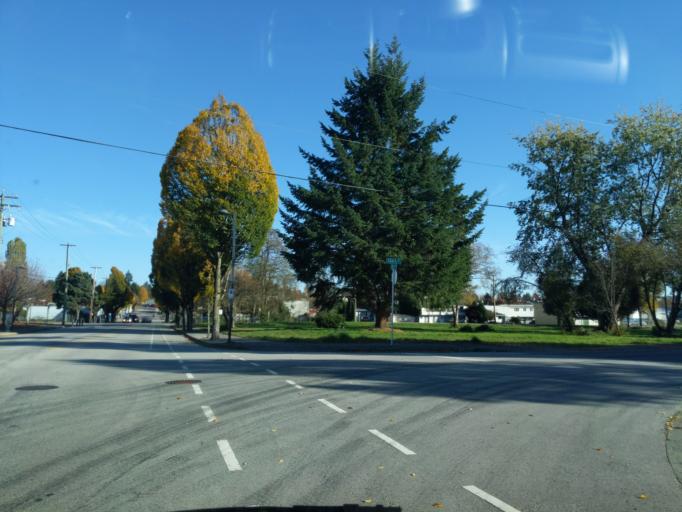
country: CA
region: British Columbia
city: New Westminster
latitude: 49.1945
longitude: -122.8497
